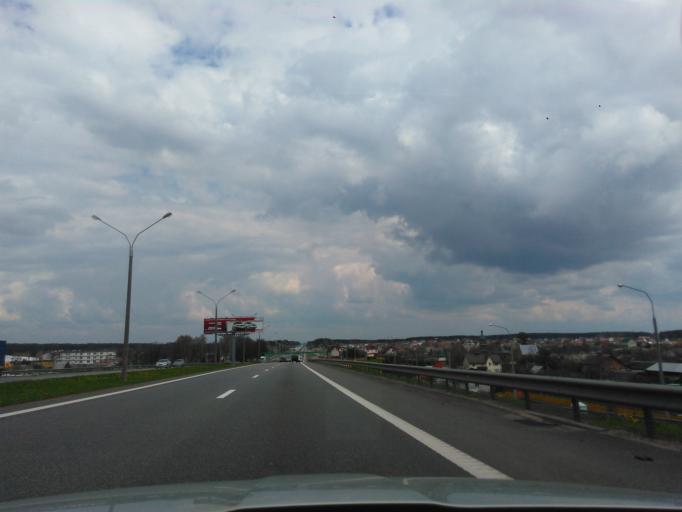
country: BY
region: Minsk
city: Korolev Stan
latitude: 53.9845
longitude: 27.7875
